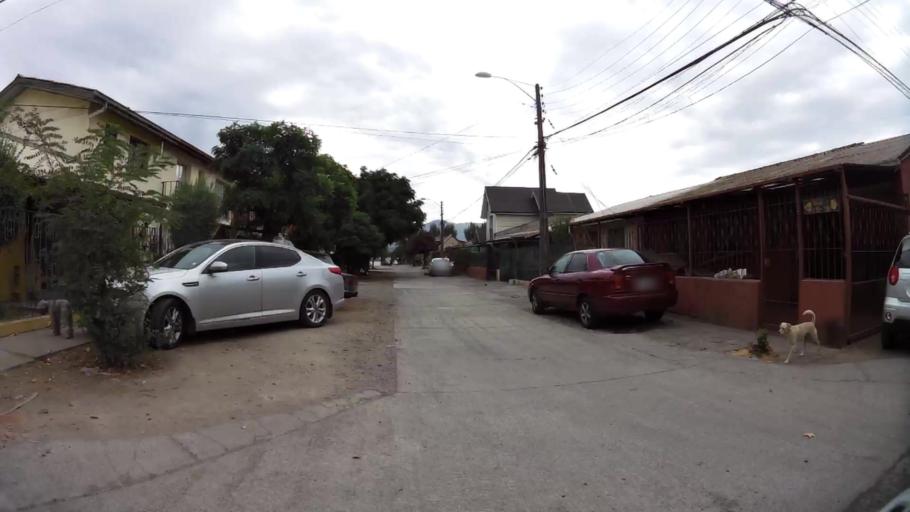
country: CL
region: O'Higgins
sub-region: Provincia de Cachapoal
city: Rancagua
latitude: -34.1596
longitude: -70.7427
